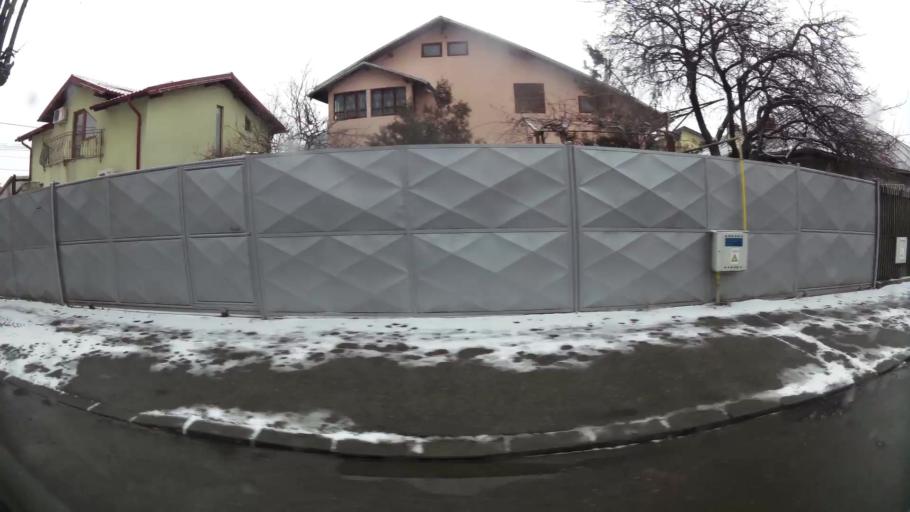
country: RO
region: Prahova
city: Ploiesti
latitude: 44.9438
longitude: 26.0047
